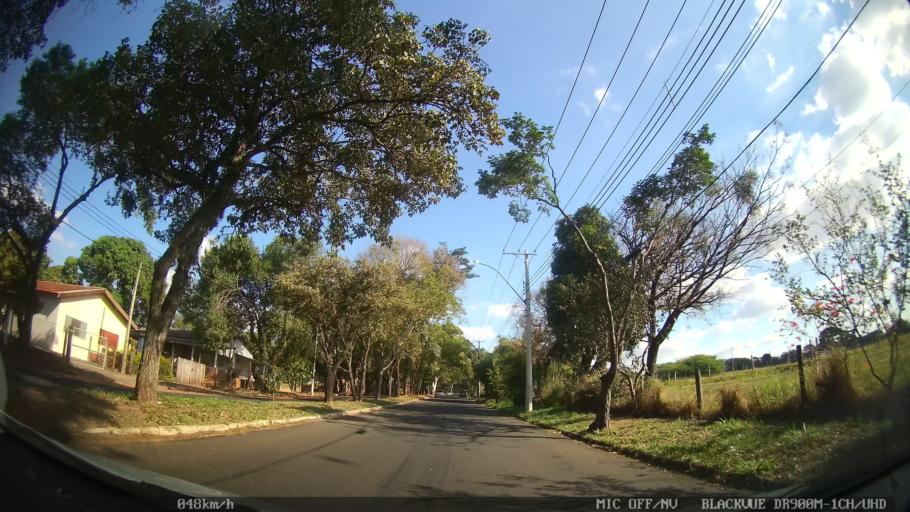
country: BR
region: Sao Paulo
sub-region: Nova Odessa
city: Nova Odessa
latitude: -22.7717
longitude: -47.3028
